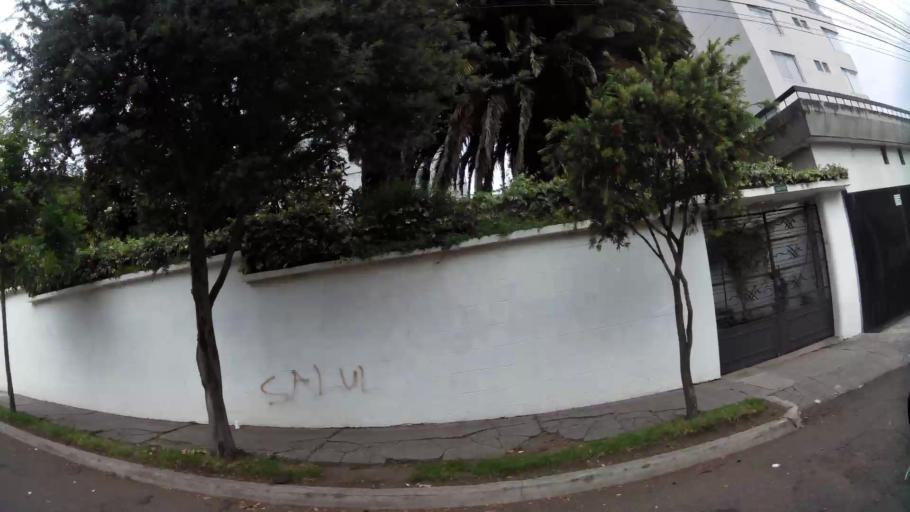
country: EC
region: Pichincha
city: Quito
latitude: -0.2097
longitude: -78.4838
